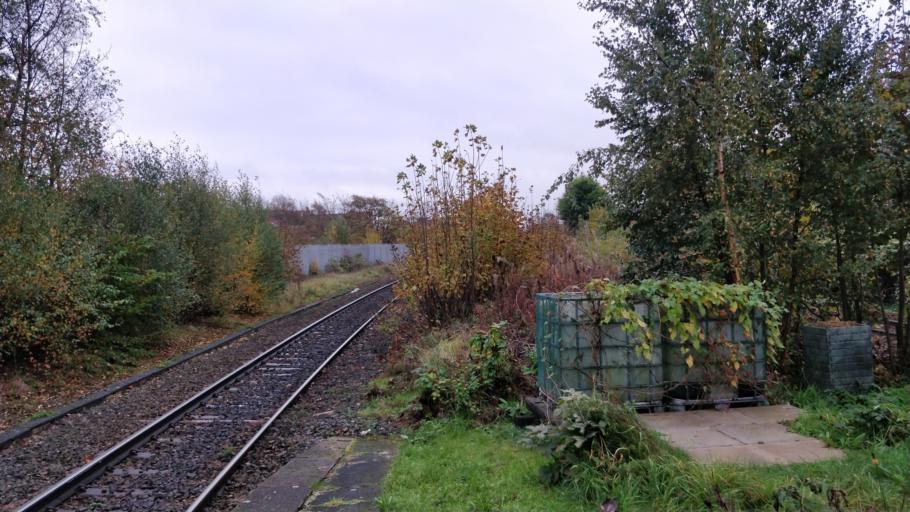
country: GB
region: England
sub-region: Sefton
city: Southport
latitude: 53.6457
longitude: -2.9749
